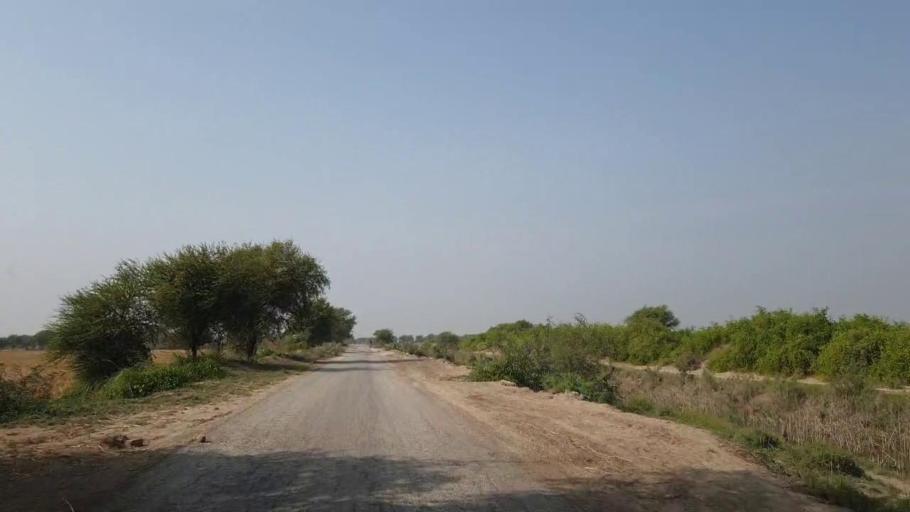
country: PK
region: Sindh
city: Matli
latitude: 24.9587
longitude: 68.5227
